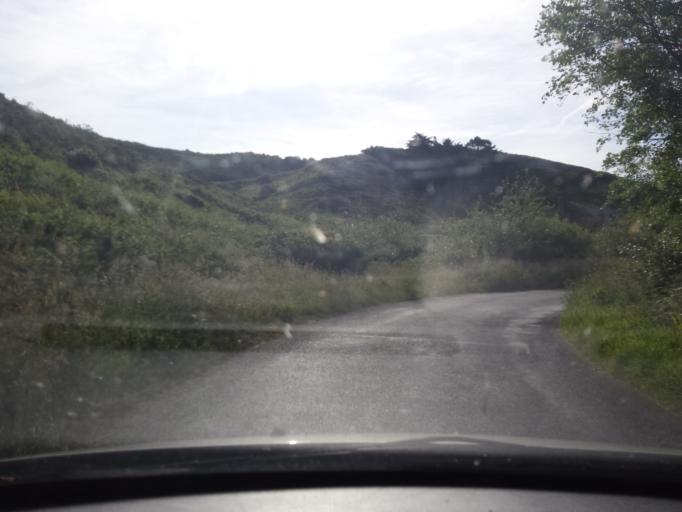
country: FR
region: Lower Normandy
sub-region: Departement de la Manche
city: Beaumont-Hague
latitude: 49.6903
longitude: -1.9332
